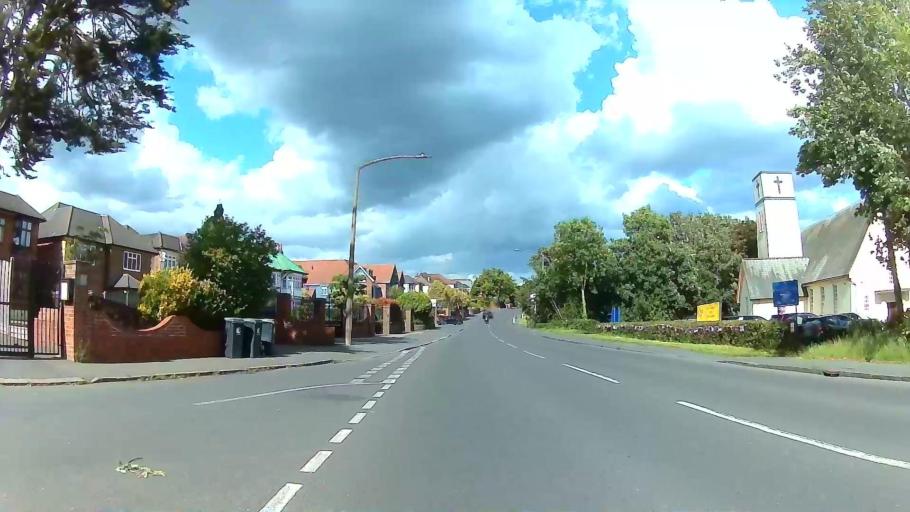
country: GB
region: England
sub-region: Essex
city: Grange Hill
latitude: 51.6111
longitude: 0.0832
